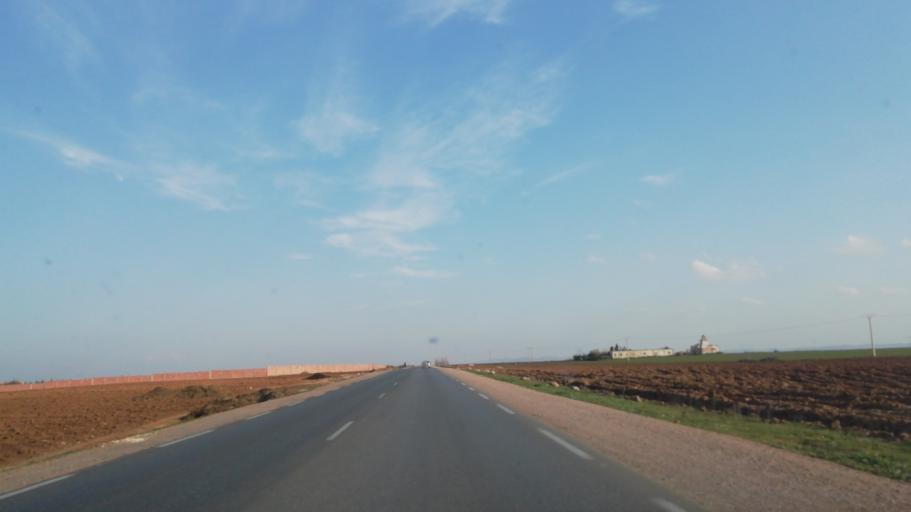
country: DZ
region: Relizane
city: Relizane
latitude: 35.8933
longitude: 0.6121
